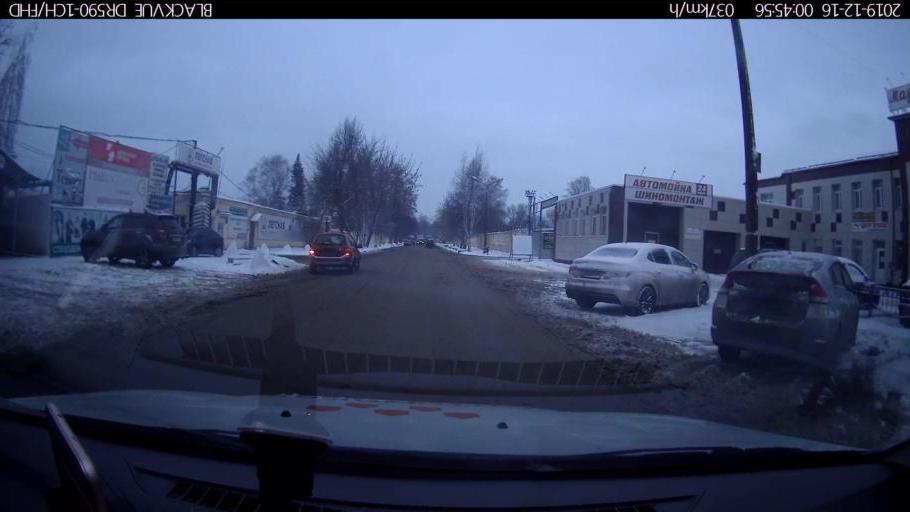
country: RU
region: Nizjnij Novgorod
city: Gorbatovka
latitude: 56.3091
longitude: 43.8585
